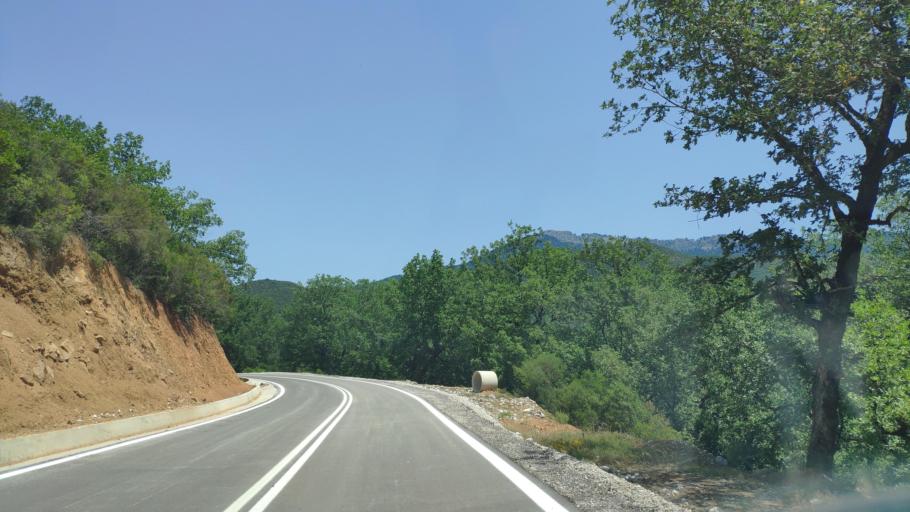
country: GR
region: Epirus
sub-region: Nomos Artas
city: Ano Kalentini
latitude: 39.1829
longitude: 21.3574
